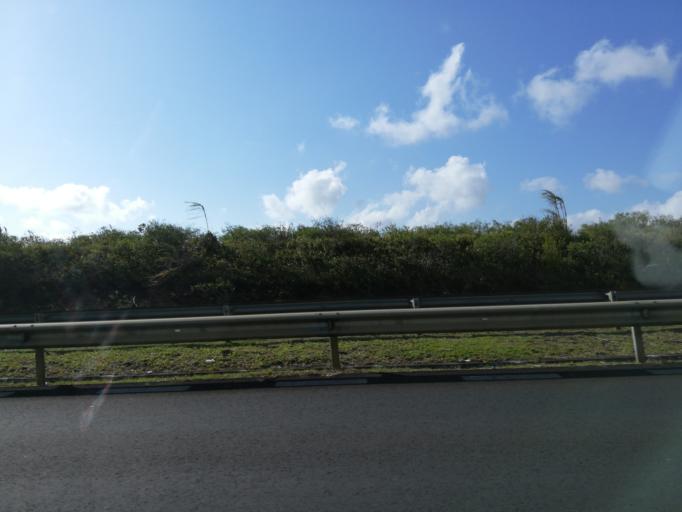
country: MU
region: Moka
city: Verdun
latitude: -20.2273
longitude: 57.5515
